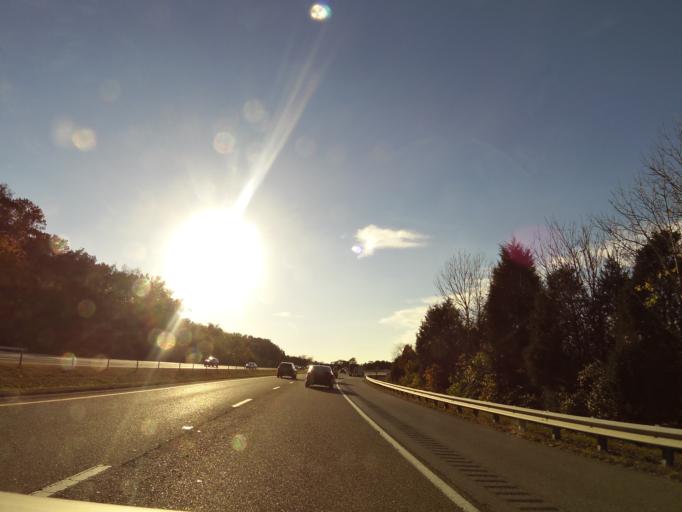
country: US
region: Tennessee
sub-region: Blount County
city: Louisville
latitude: 35.8586
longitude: -84.0649
